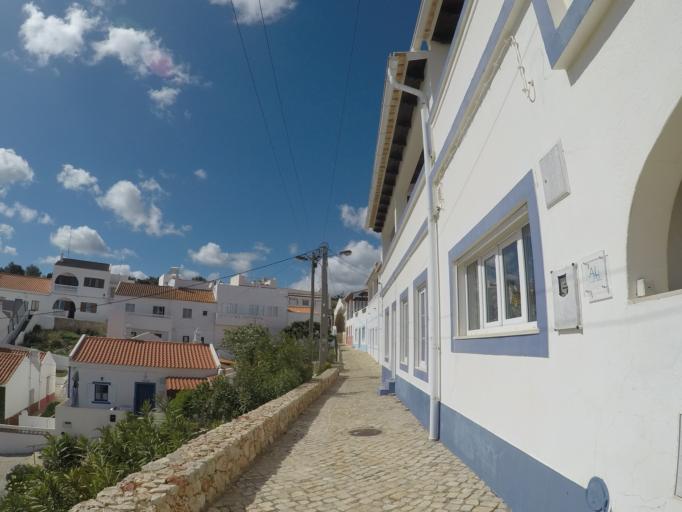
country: PT
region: Faro
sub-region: Vila do Bispo
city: Vila do Bispo
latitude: 37.0662
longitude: -8.8219
